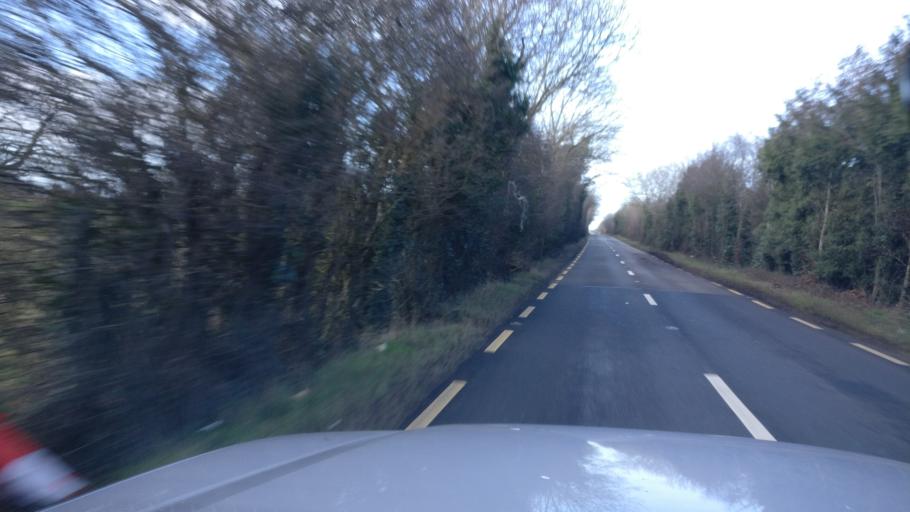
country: IE
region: Leinster
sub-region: Laois
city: Mountmellick
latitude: 53.0786
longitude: -7.3309
